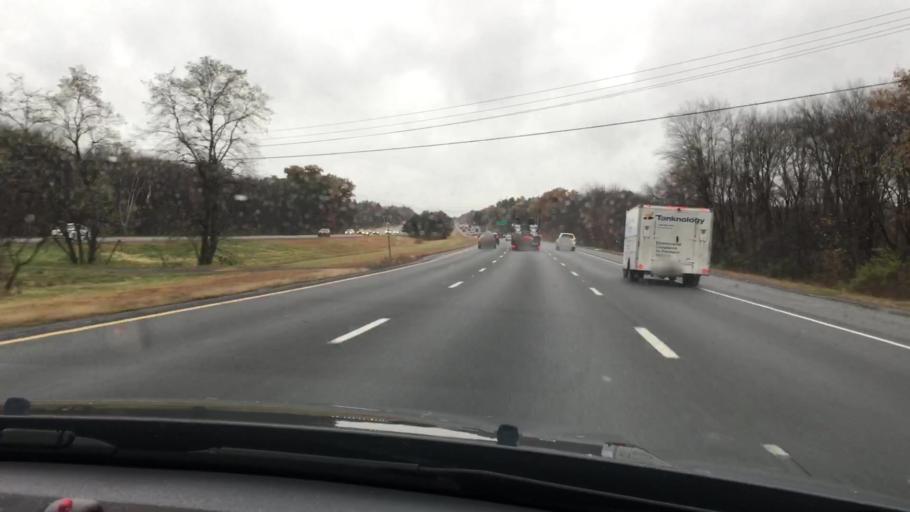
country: US
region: Massachusetts
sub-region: Middlesex County
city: Westford
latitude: 42.5744
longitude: -71.4189
